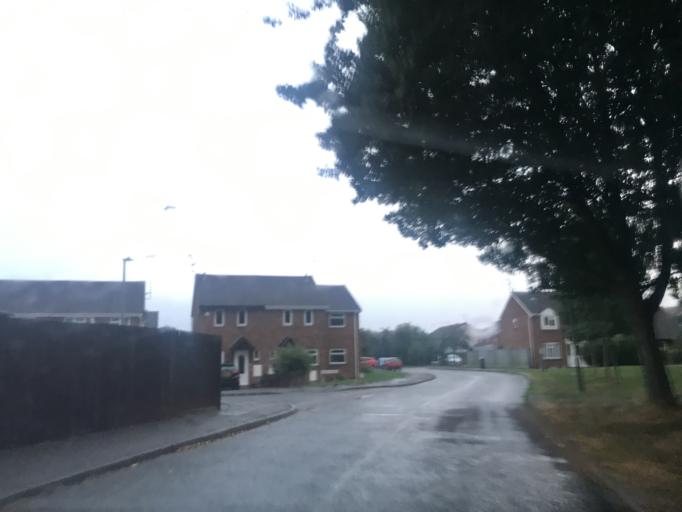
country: GB
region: England
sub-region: Buckinghamshire
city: Aylesbury
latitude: 51.8252
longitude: -0.7950
